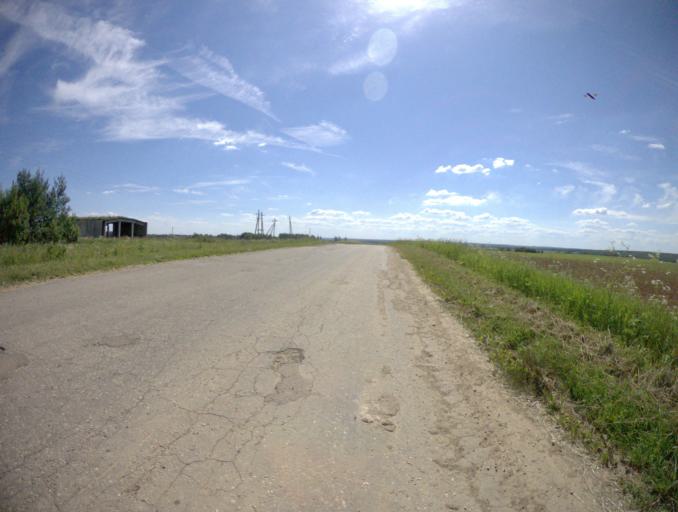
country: RU
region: Vladimir
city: Stavrovo
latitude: 56.2504
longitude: 40.0333
